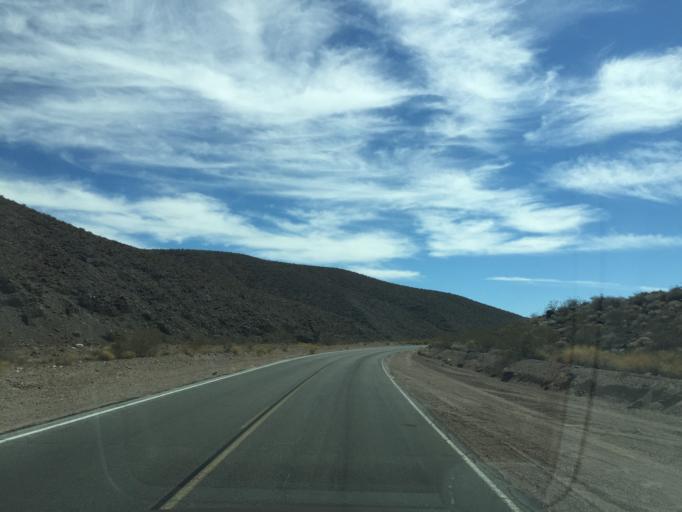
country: US
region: Nevada
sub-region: Nye County
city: Beatty
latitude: 36.2830
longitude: -116.6720
